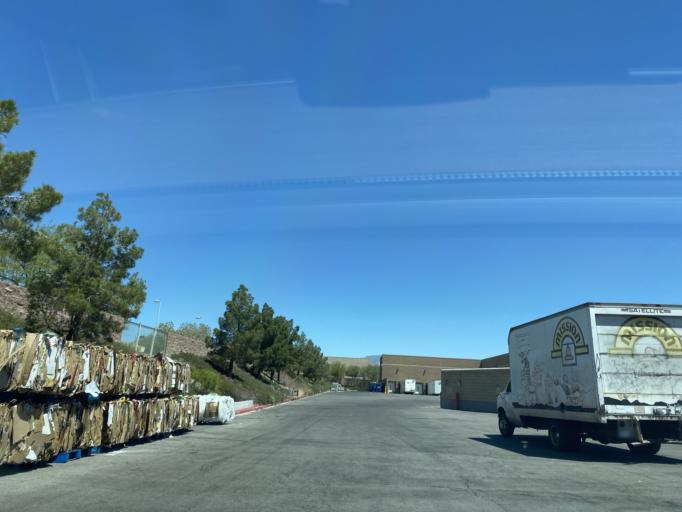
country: US
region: Nevada
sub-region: Clark County
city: Summerlin South
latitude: 36.2722
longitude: -115.2719
